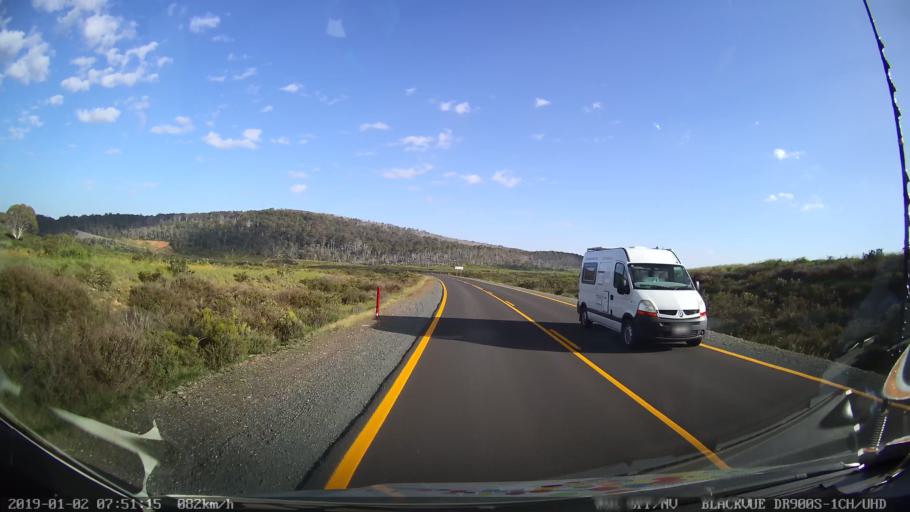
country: AU
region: New South Wales
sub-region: Tumut Shire
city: Tumut
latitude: -35.7205
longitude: 148.5311
